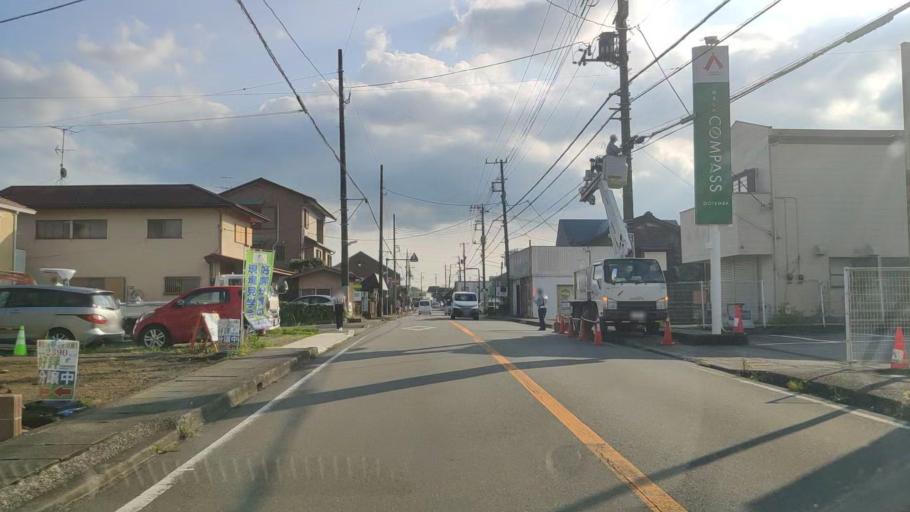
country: JP
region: Shizuoka
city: Gotemba
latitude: 35.3134
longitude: 138.9402
